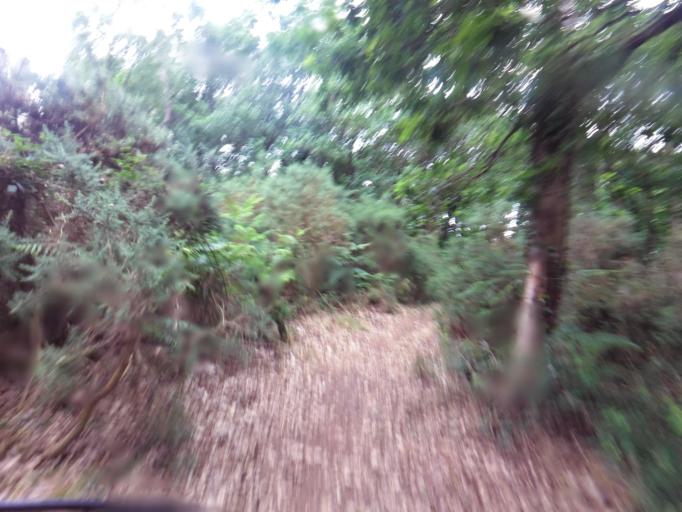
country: FR
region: Brittany
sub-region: Departement du Morbihan
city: Molac
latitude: 47.7620
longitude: -2.4185
